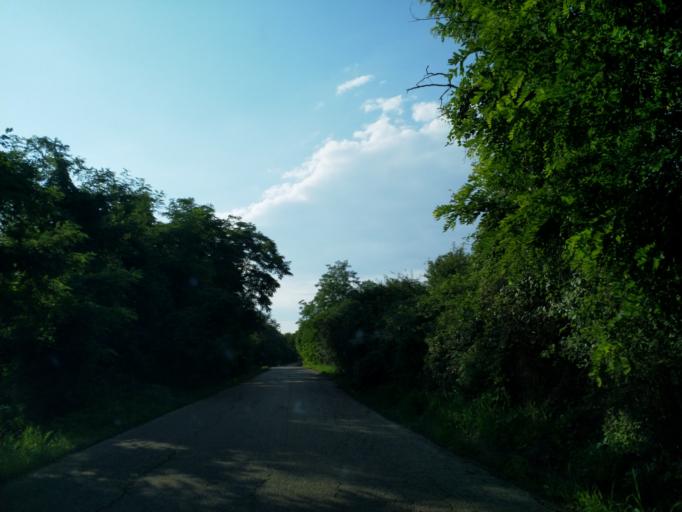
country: RS
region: Central Serbia
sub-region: Pomoravski Okrug
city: Jagodina
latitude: 43.9983
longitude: 21.1909
